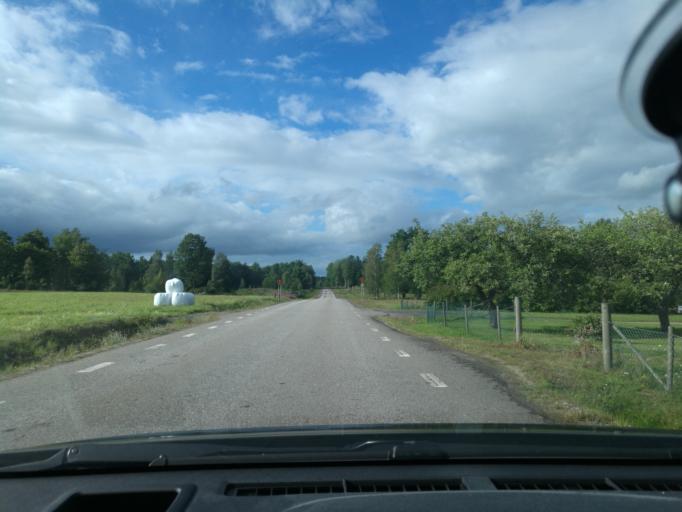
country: SE
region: Kronoberg
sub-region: Vaxjo Kommun
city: Braas
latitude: 57.1131
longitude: 14.9774
